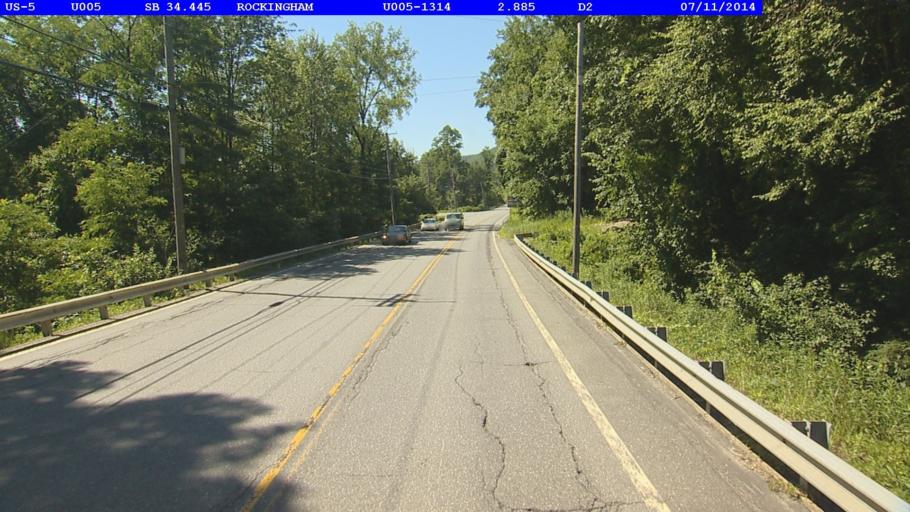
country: US
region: Vermont
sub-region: Windham County
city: Bellows Falls
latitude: 43.1626
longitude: -72.4567
